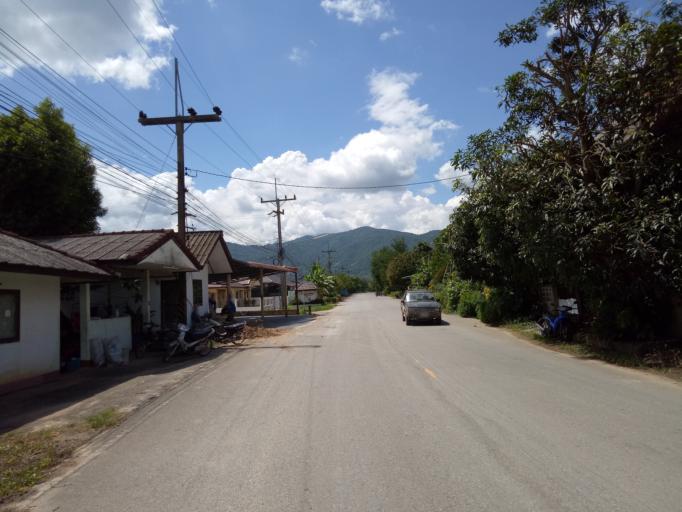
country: TH
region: Chiang Rai
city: Chiang Rai
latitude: 19.9930
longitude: 99.8259
